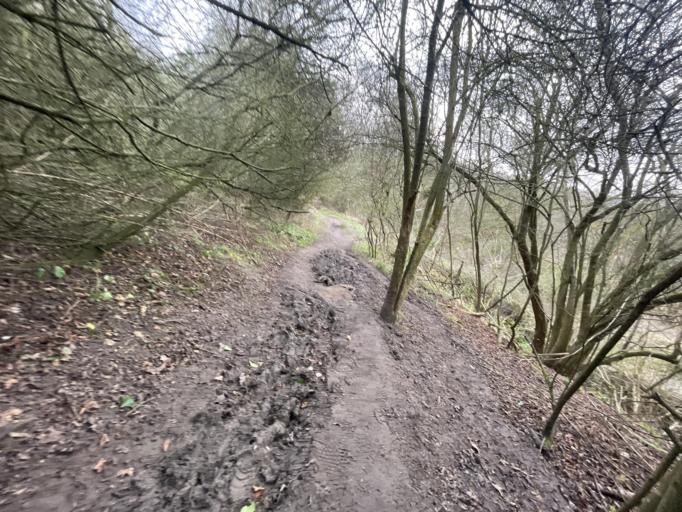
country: GB
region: England
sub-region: West Berkshire
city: Calcot
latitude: 51.4544
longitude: -1.0652
